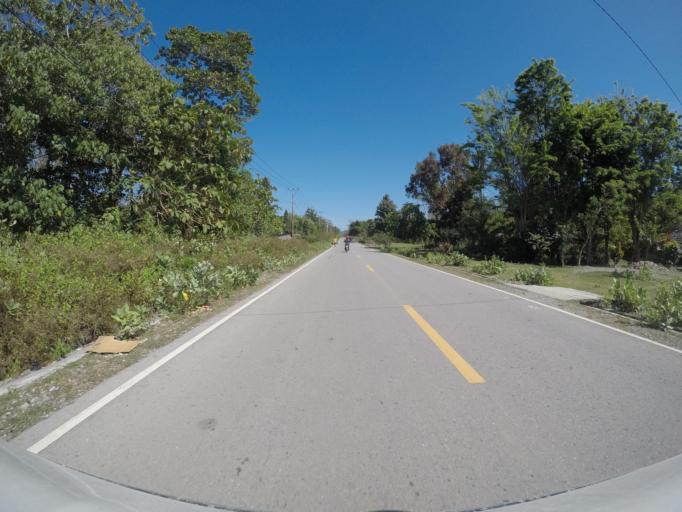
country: TL
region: Viqueque
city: Viqueque
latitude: -8.9749
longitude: 126.0386
